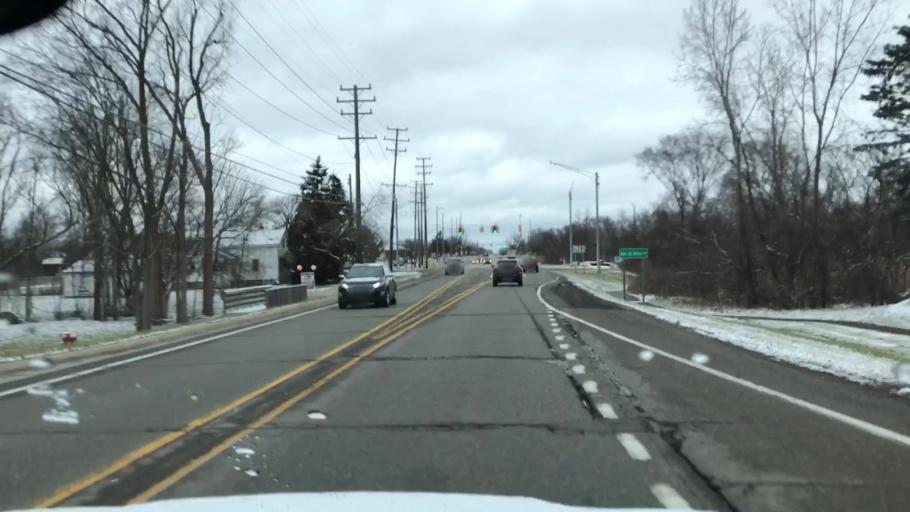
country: US
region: Michigan
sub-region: Oakland County
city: Novi
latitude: 42.4626
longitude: -83.4745
